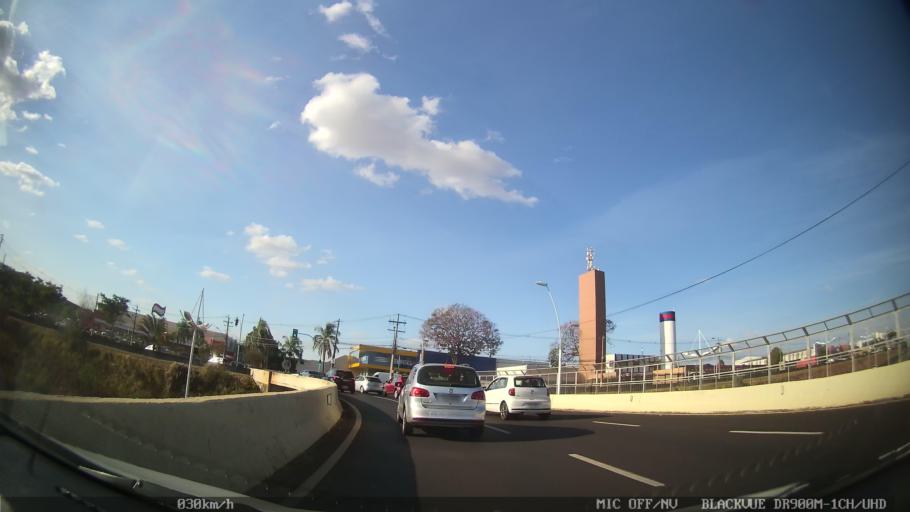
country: BR
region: Sao Paulo
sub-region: Ribeirao Preto
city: Ribeirao Preto
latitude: -21.1940
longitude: -47.7758
